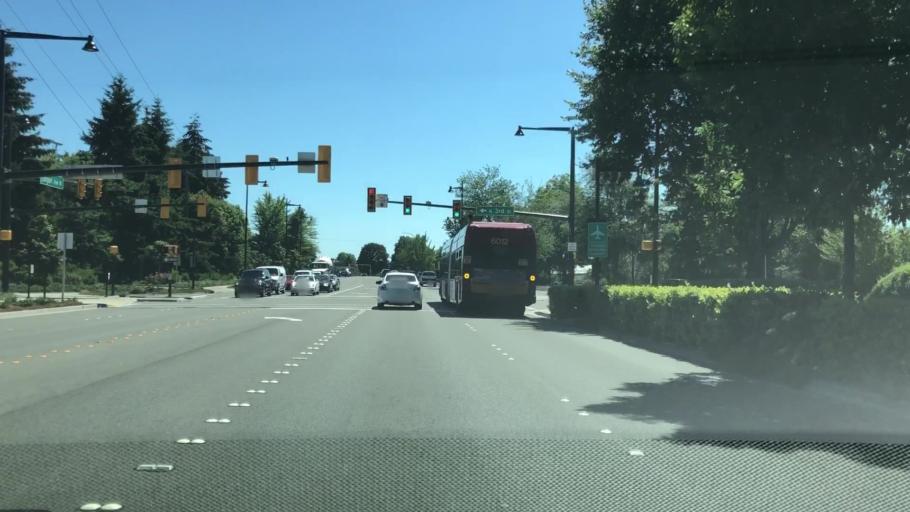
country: US
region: Washington
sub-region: King County
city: Renton
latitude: 47.4875
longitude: -122.2084
